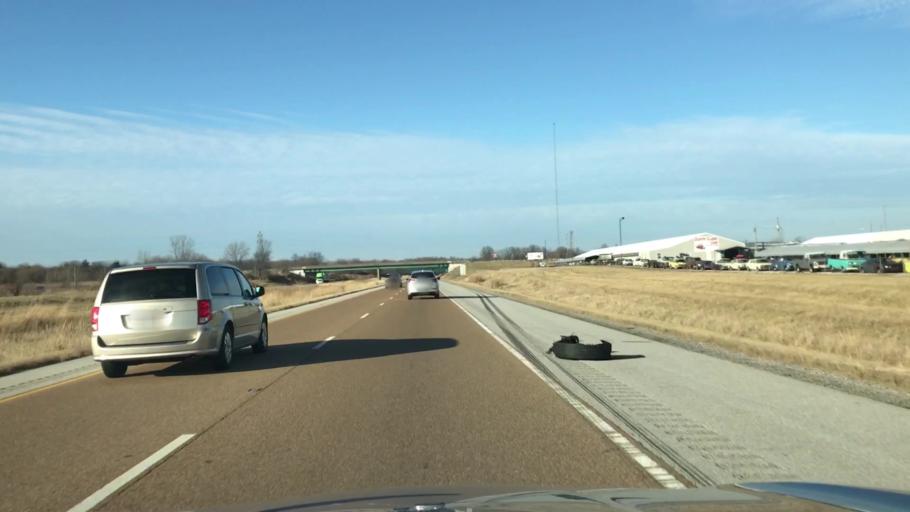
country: US
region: Illinois
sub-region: Macoupin County
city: Staunton
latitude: 39.0290
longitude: -89.7516
